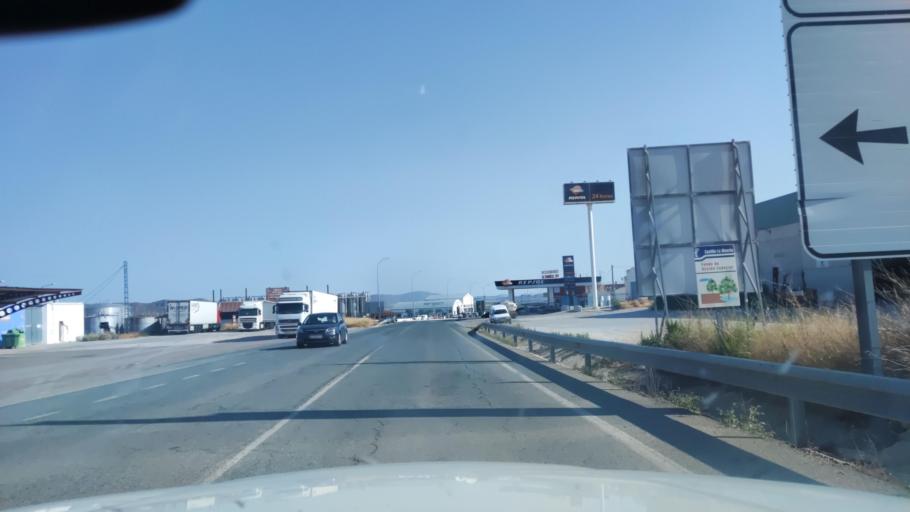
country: ES
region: Castille-La Mancha
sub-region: Provincia de Albacete
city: Tobarra
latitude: 38.6036
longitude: -1.6811
